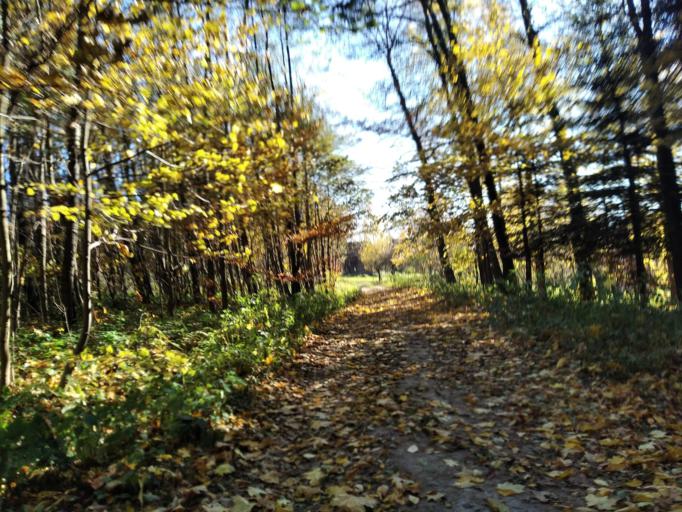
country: PL
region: Subcarpathian Voivodeship
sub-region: Powiat krosnienski
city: Leki
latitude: 49.8284
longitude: 21.6579
